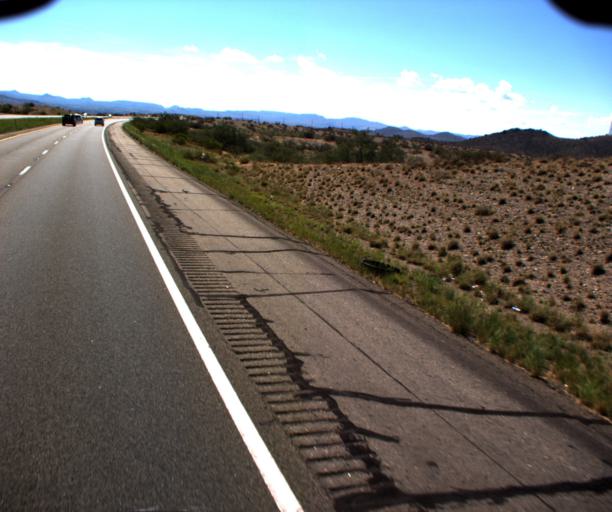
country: US
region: Arizona
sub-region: Yavapai County
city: Spring Valley
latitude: 34.3475
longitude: -112.1476
